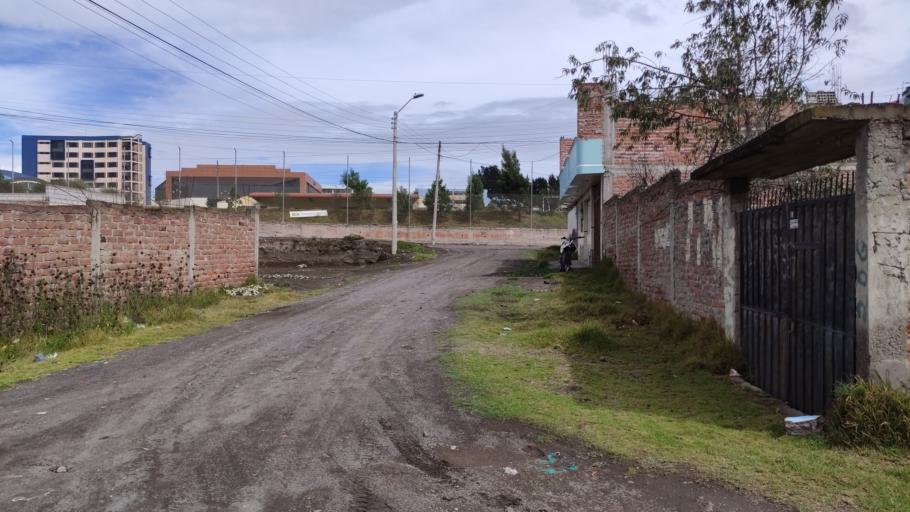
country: EC
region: Chimborazo
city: Riobamba
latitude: -1.6540
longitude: -78.6407
